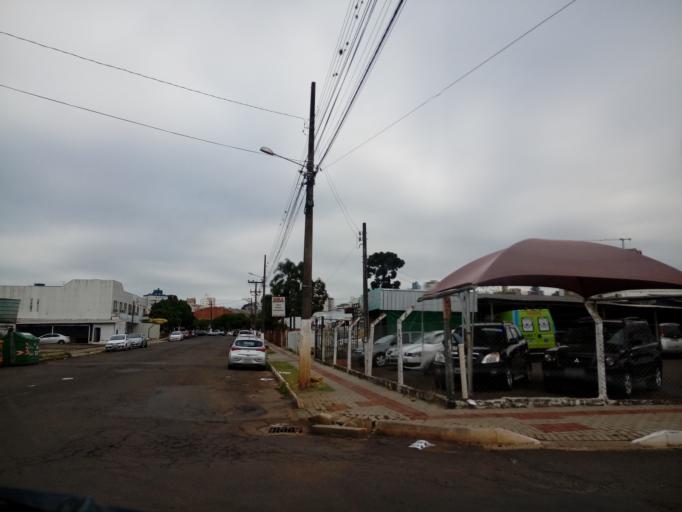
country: BR
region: Santa Catarina
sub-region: Chapeco
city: Chapeco
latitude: -27.0917
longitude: -52.6215
